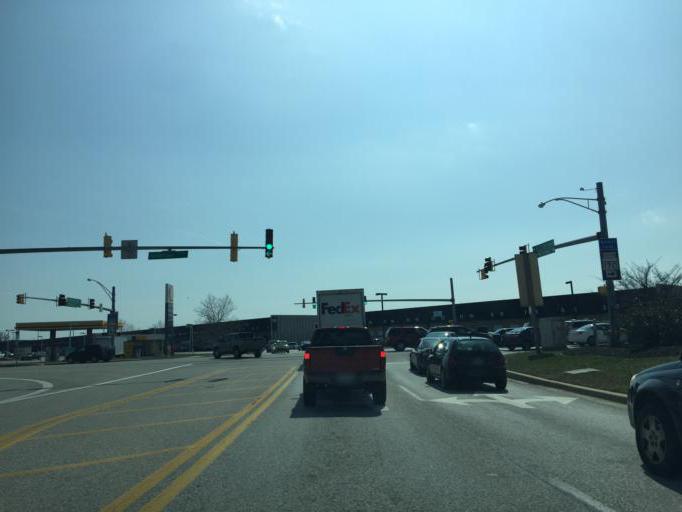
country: US
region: Maryland
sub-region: Anne Arundel County
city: Linthicum
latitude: 39.1907
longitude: -76.6712
